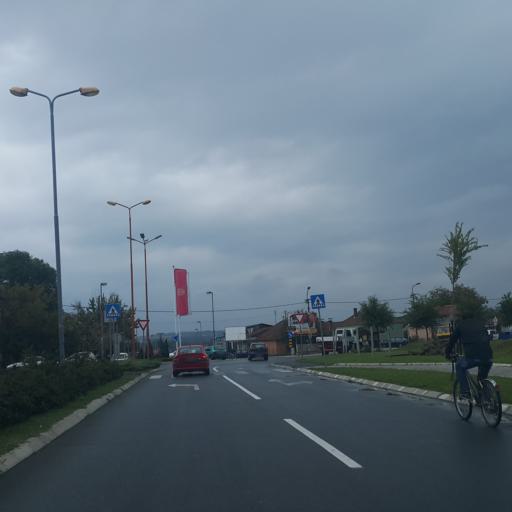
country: RS
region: Central Serbia
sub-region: Rasinski Okrug
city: Krusevac
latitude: 43.5706
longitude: 21.3397
